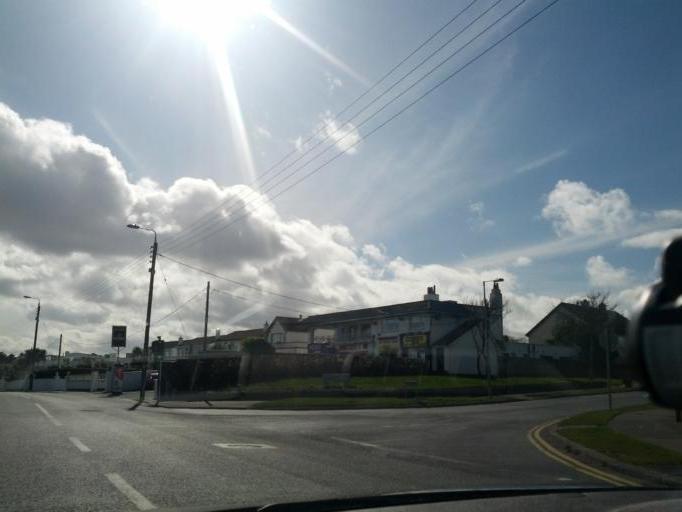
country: IE
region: Leinster
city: Portmarnock
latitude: 53.4341
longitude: -6.1239
